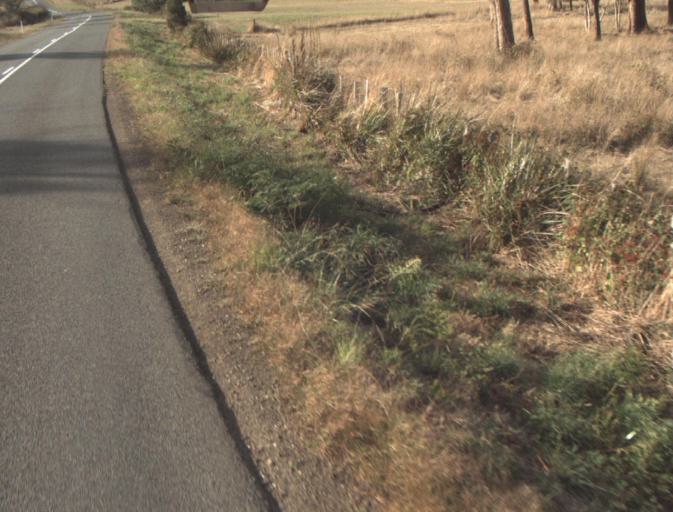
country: AU
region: Tasmania
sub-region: Launceston
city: Mayfield
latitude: -41.2197
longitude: 147.1215
